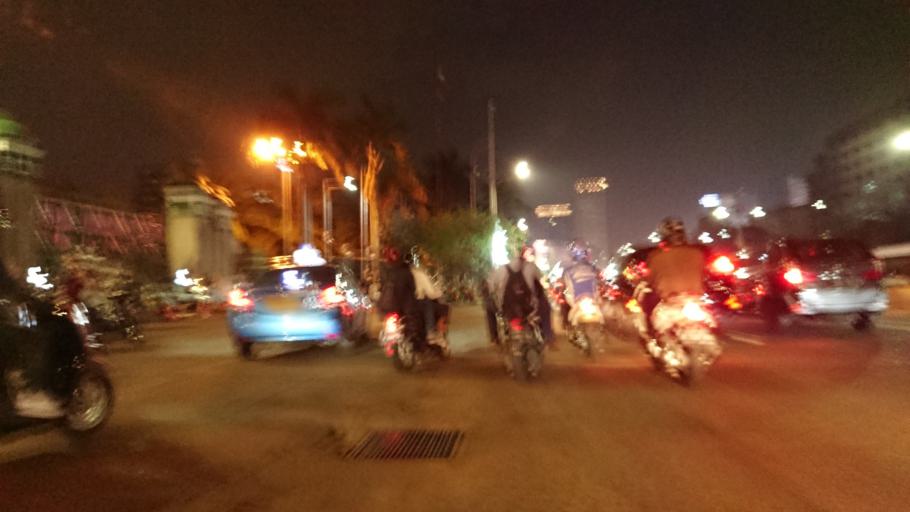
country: ID
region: Jakarta Raya
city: Jakarta
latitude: -6.2080
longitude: 106.8032
